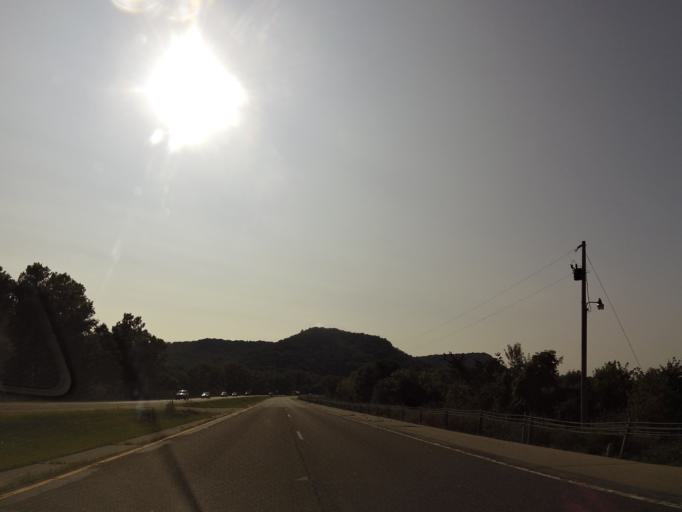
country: US
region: Wisconsin
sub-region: Trempealeau County
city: Trempealeau
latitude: 44.0067
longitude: -91.4883
